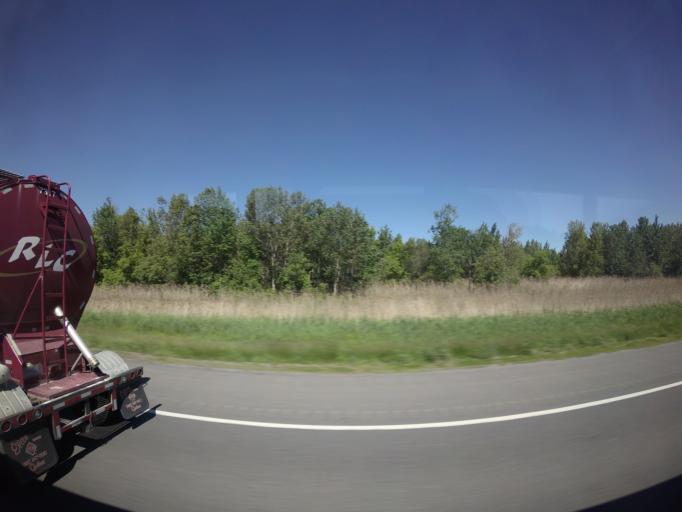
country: CA
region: Quebec
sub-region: Mauricie
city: Saint-Germain-de-Grantham
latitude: 45.7812
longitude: -72.6706
